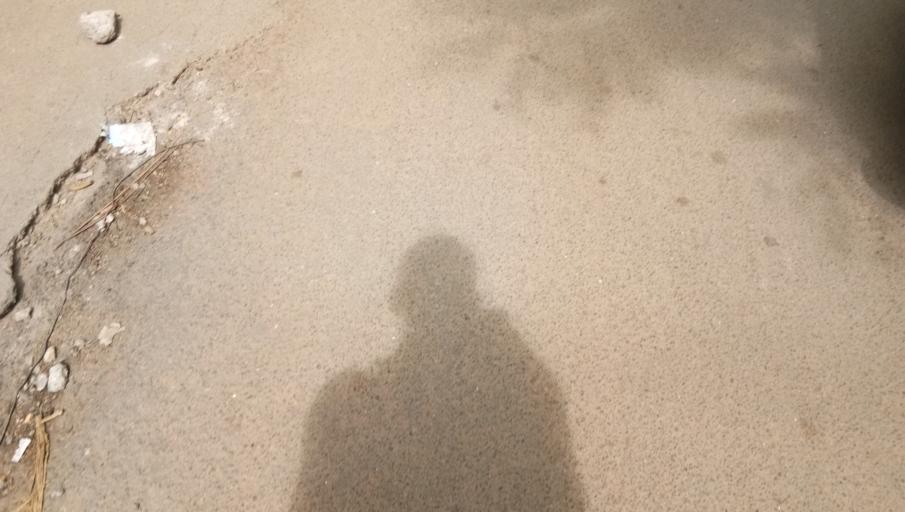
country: IN
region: Telangana
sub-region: Rangareddi
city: Kukatpalli
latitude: 17.4995
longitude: 78.4015
